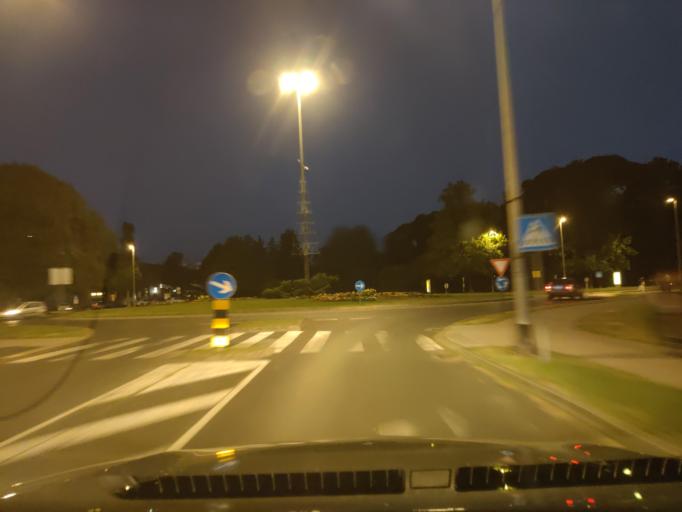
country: HR
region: Medimurska
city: Cakovec
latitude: 46.3916
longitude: 16.4333
